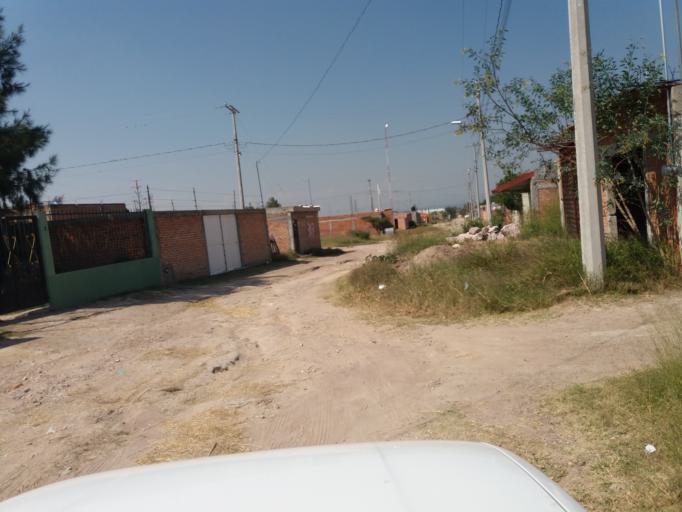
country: MX
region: Aguascalientes
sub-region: Aguascalientes
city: Penuelas (El Cienegal)
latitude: 21.7527
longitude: -102.2617
